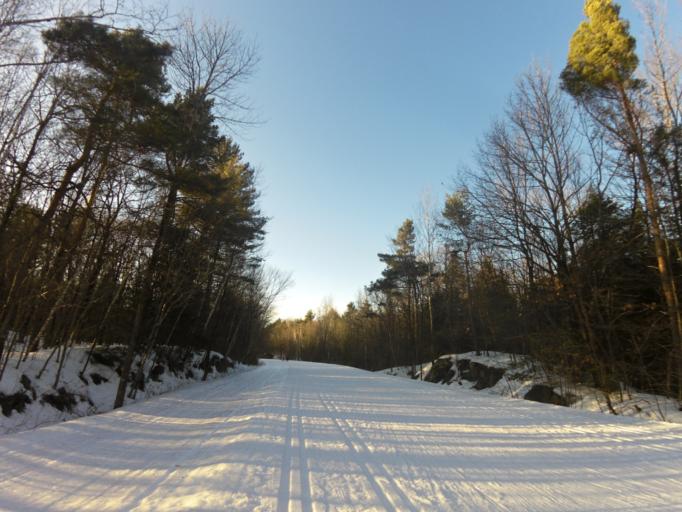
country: CA
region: Quebec
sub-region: Outaouais
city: Gatineau
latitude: 45.5237
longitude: -75.8343
